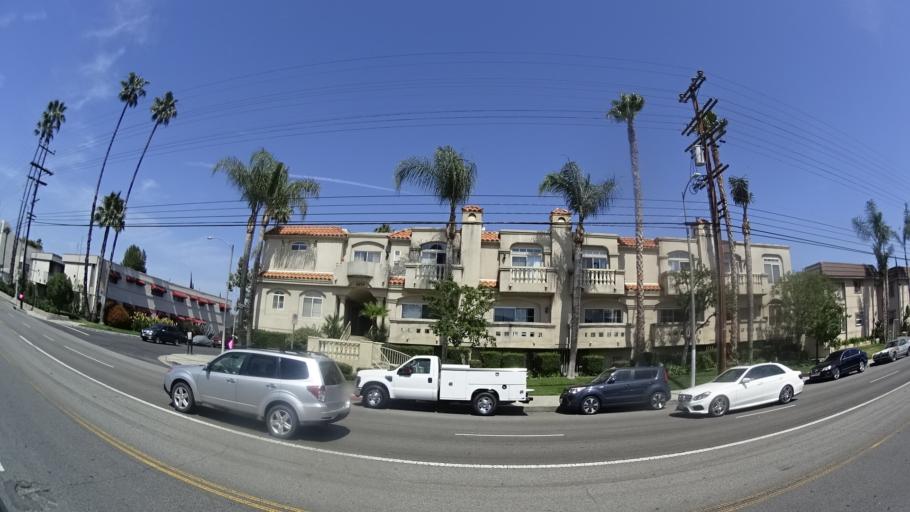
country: US
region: California
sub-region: Los Angeles County
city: Sherman Oaks
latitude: 34.1610
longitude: -118.4575
